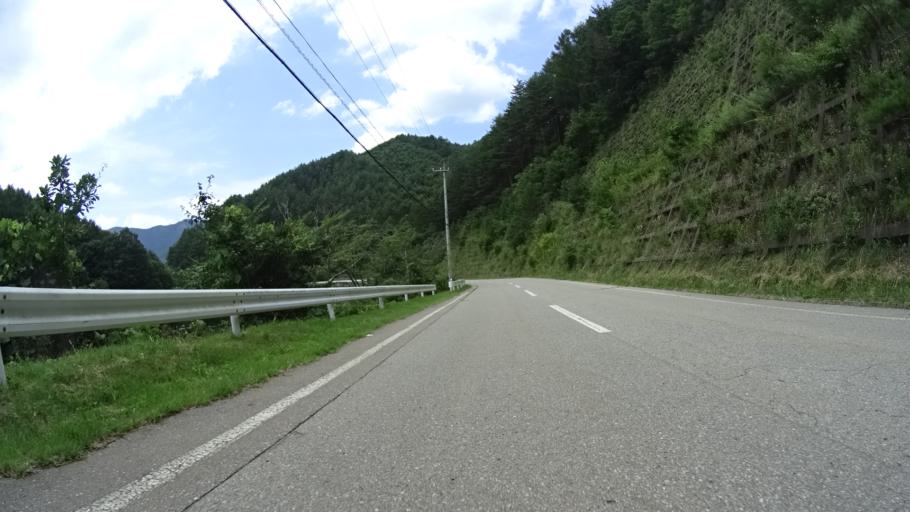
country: JP
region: Nagano
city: Saku
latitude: 36.0711
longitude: 138.6151
